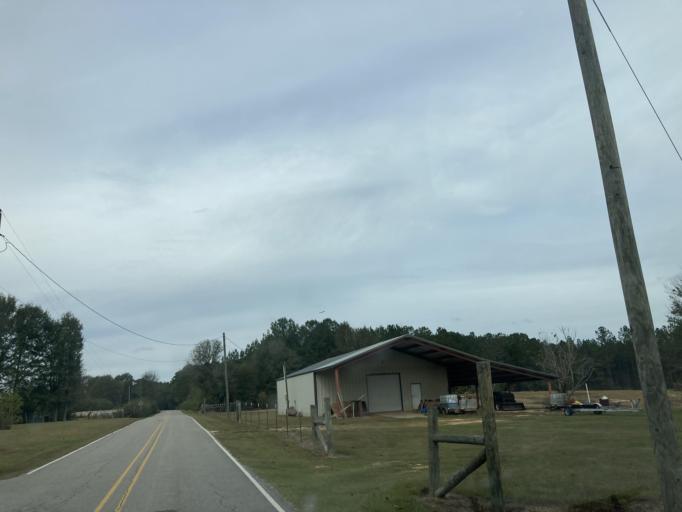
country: US
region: Mississippi
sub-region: Lamar County
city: Purvis
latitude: 31.1140
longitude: -89.4817
